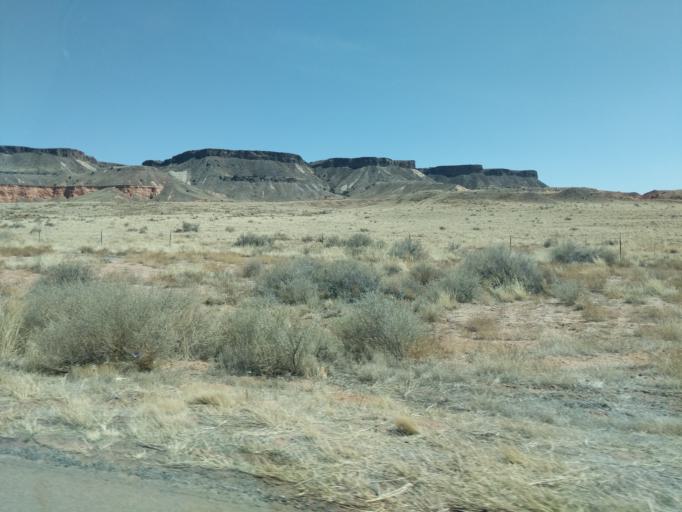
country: US
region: Arizona
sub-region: Navajo County
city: Dilkon
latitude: 35.4281
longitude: -110.0656
